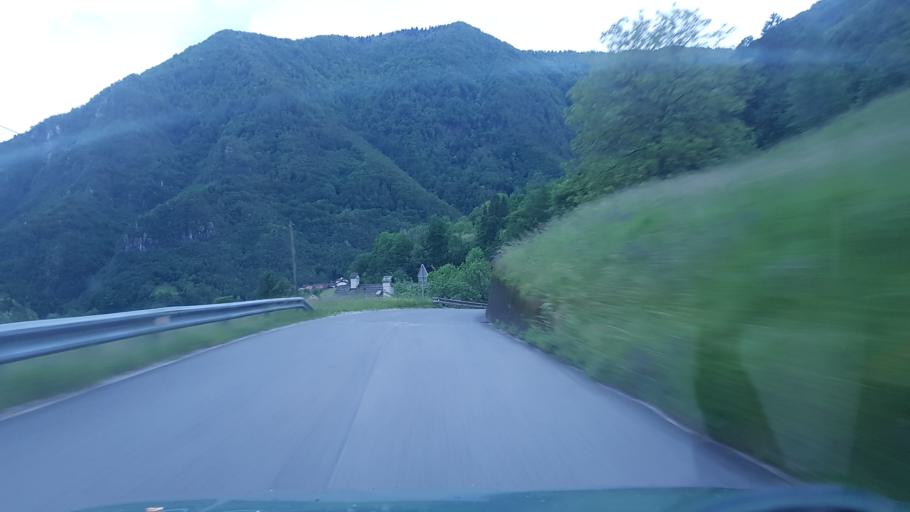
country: SI
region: Cerkno
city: Cerkno
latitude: 46.1630
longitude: 13.8831
